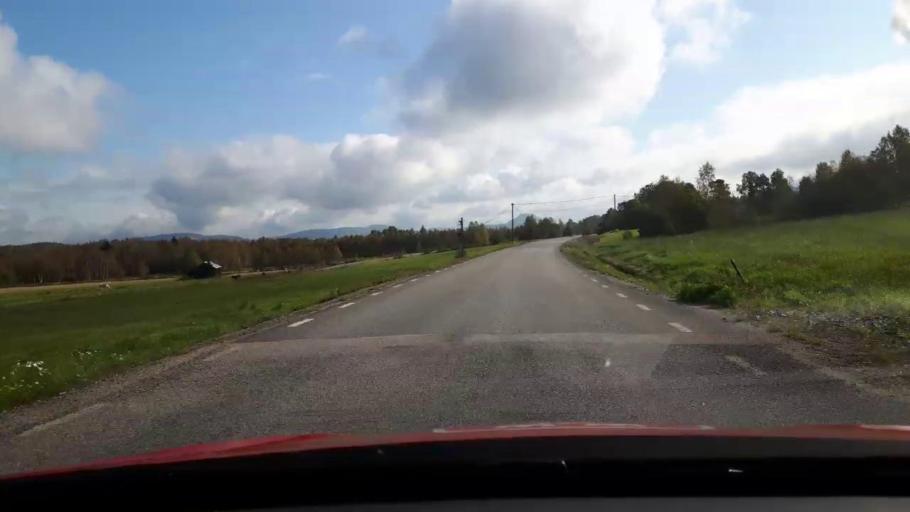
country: SE
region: Gaevleborg
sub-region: Ljusdals Kommun
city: Ljusdal
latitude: 61.7603
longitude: 16.0911
